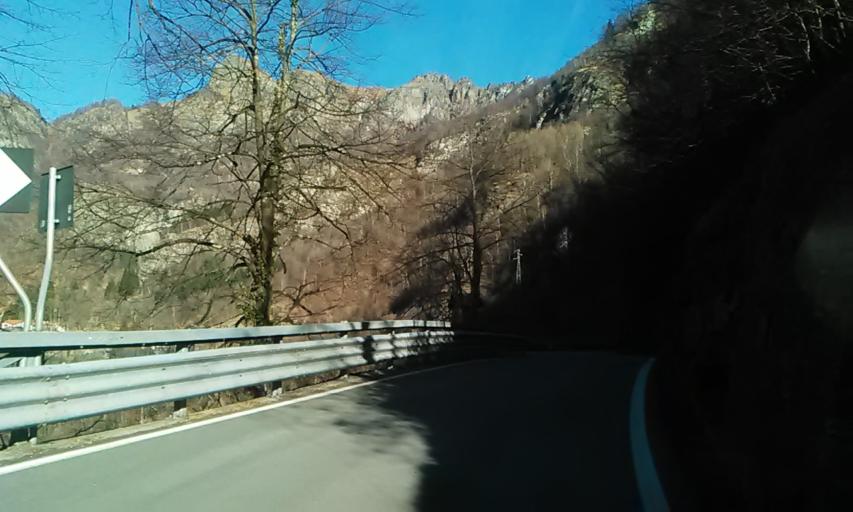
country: IT
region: Piedmont
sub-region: Provincia di Vercelli
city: Boccioleto
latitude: 45.8339
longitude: 8.0873
